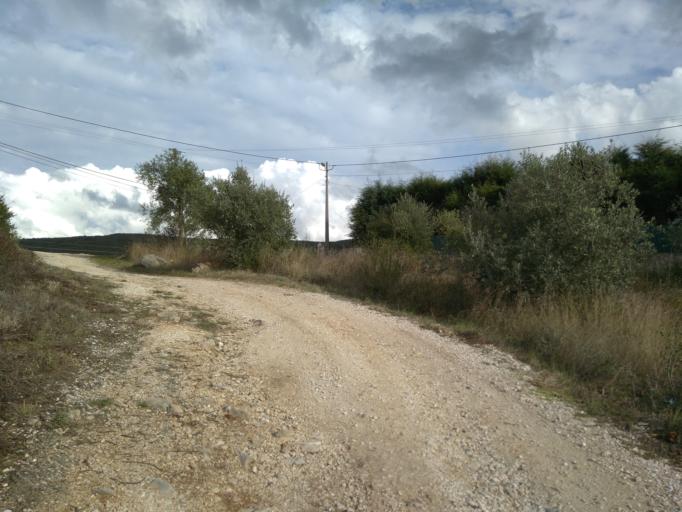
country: PT
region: Leiria
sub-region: Porto de Mos
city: Porto de Mos
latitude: 39.5983
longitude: -8.8111
